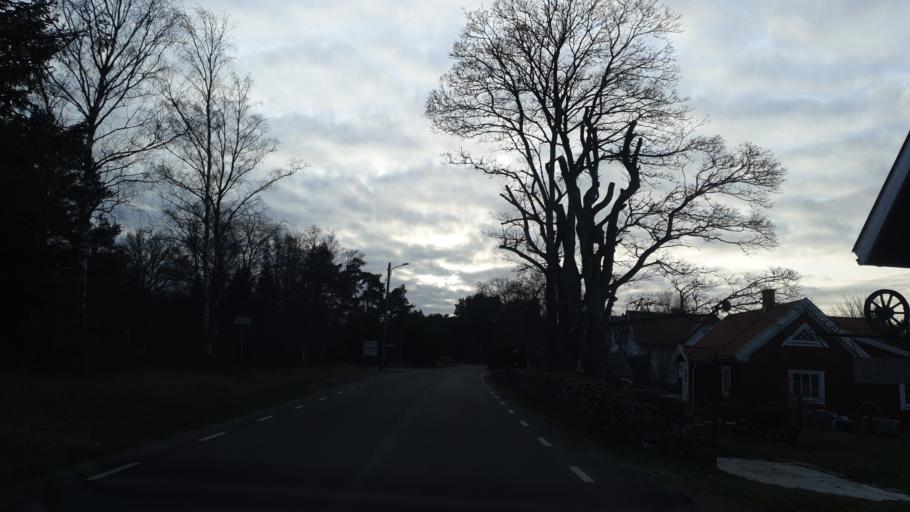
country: SE
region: Blekinge
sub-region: Karlskrona Kommun
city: Jaemjoe
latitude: 56.2118
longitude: 15.9674
